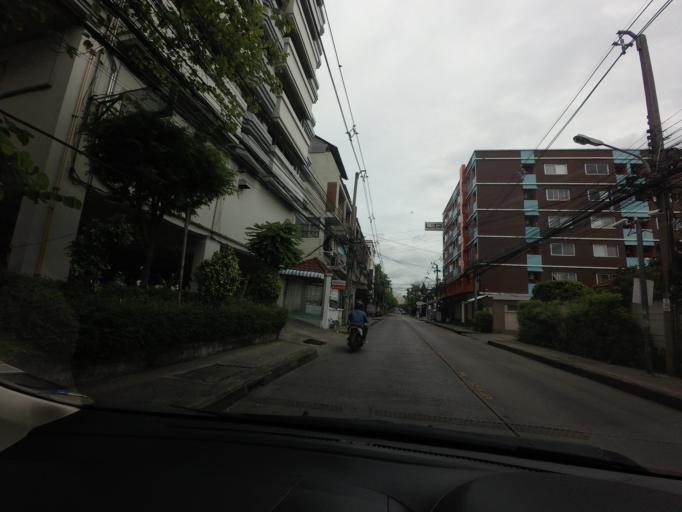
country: TH
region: Bangkok
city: Wang Thonglang
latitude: 13.7711
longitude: 100.6224
